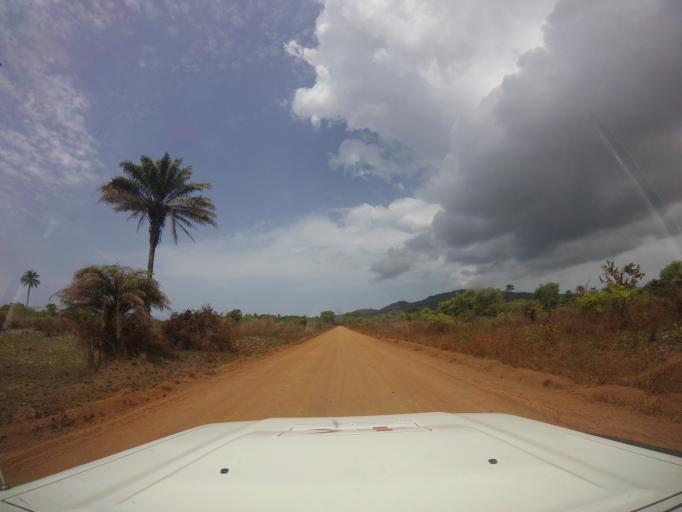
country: LR
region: Grand Cape Mount
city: Robertsport
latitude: 6.7047
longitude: -11.3276
